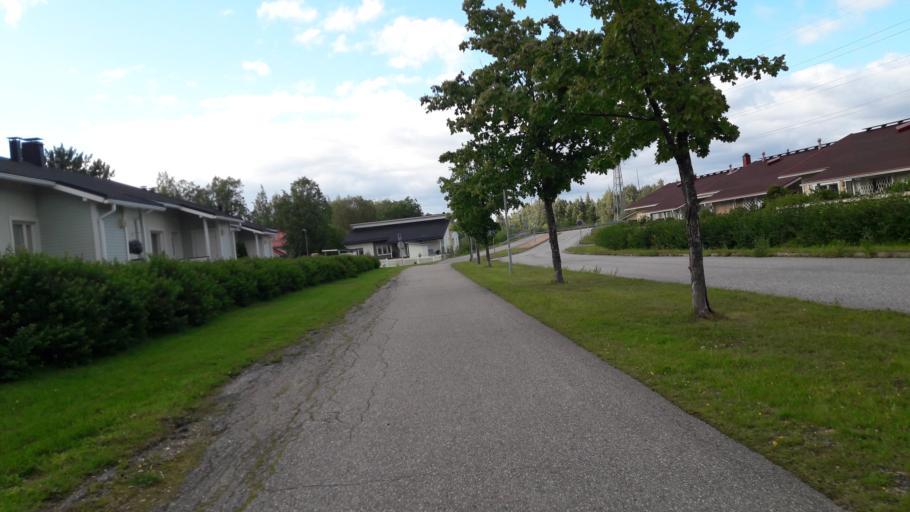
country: FI
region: North Karelia
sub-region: Joensuu
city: Joensuu
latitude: 62.5967
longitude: 29.7942
